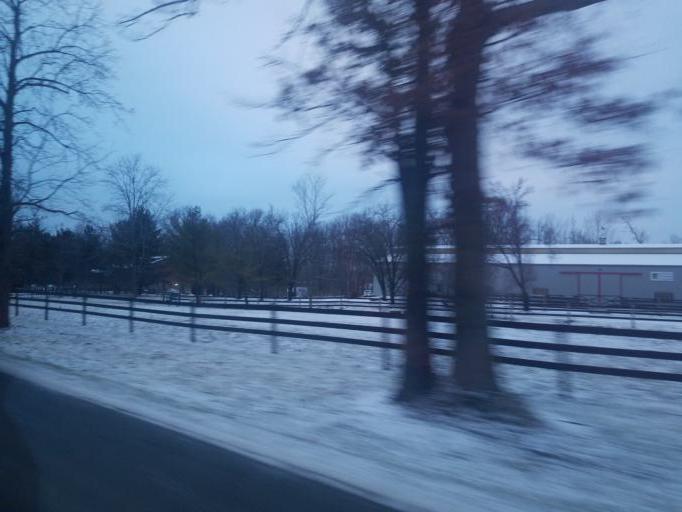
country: US
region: Ohio
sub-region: Delaware County
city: Sunbury
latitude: 40.1680
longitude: -82.8578
